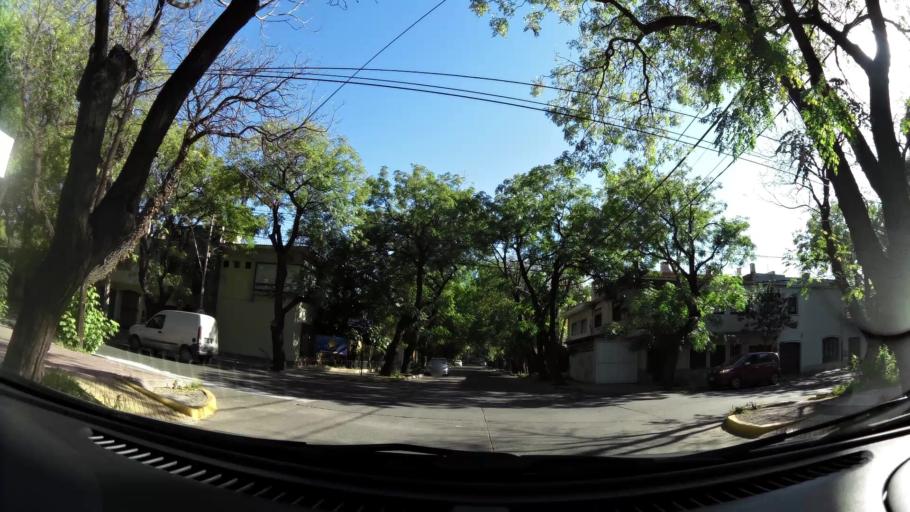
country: AR
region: Mendoza
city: Las Heras
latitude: -32.8704
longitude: -68.8517
